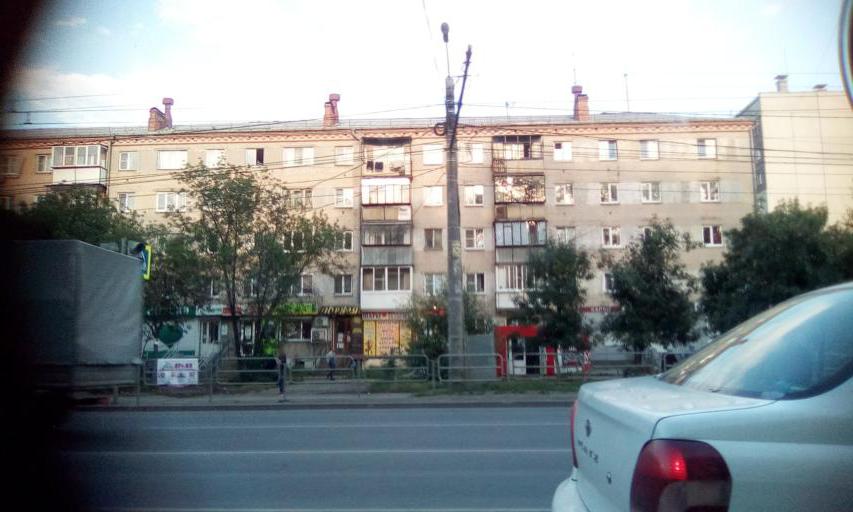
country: RU
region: Chelyabinsk
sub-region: Gorod Chelyabinsk
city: Chelyabinsk
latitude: 55.1245
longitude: 61.3642
